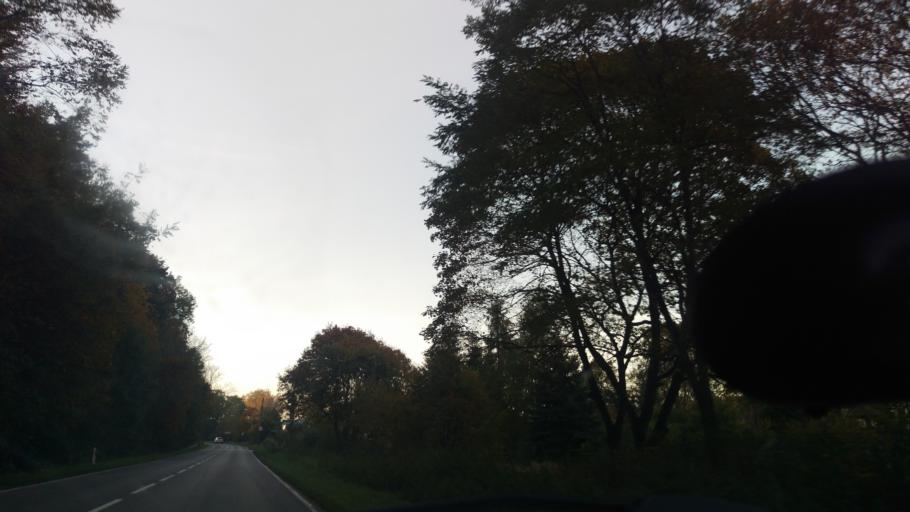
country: PL
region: West Pomeranian Voivodeship
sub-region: Powiat gryfinski
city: Stare Czarnowo
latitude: 53.3410
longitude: 14.7607
